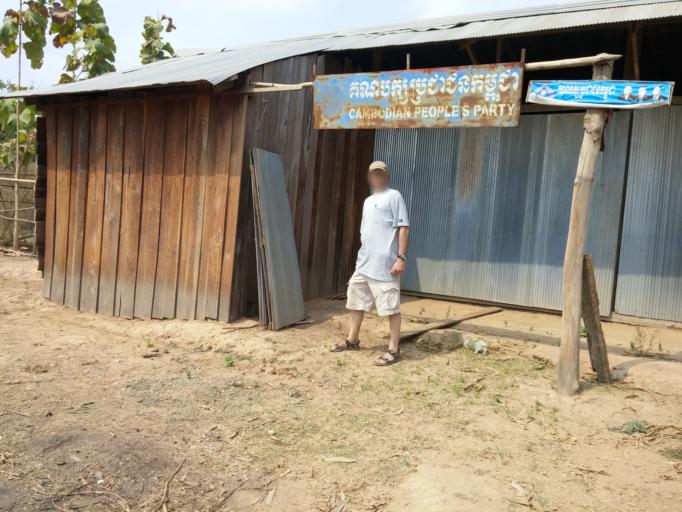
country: LA
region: Champasak
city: Khong
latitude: 14.0950
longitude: 105.7405
